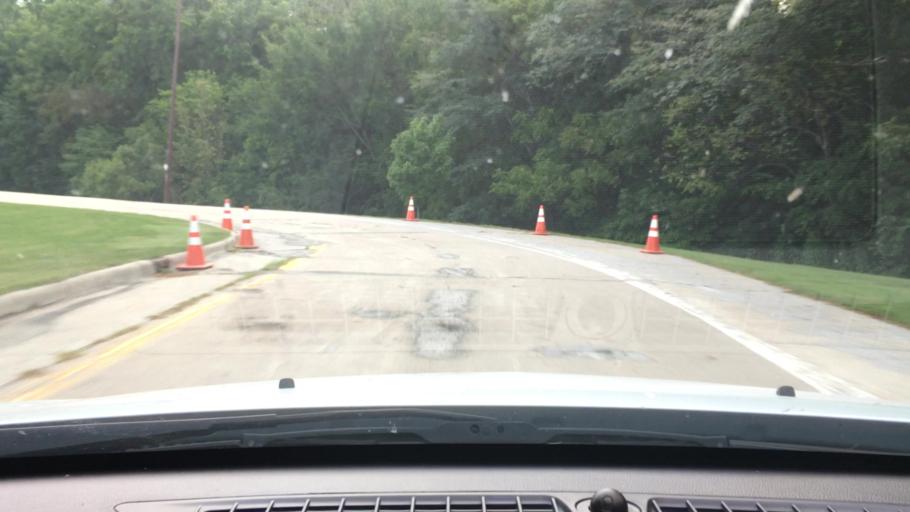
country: US
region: Illinois
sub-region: McLean County
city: Twin Grove
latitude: 40.3585
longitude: -89.1104
